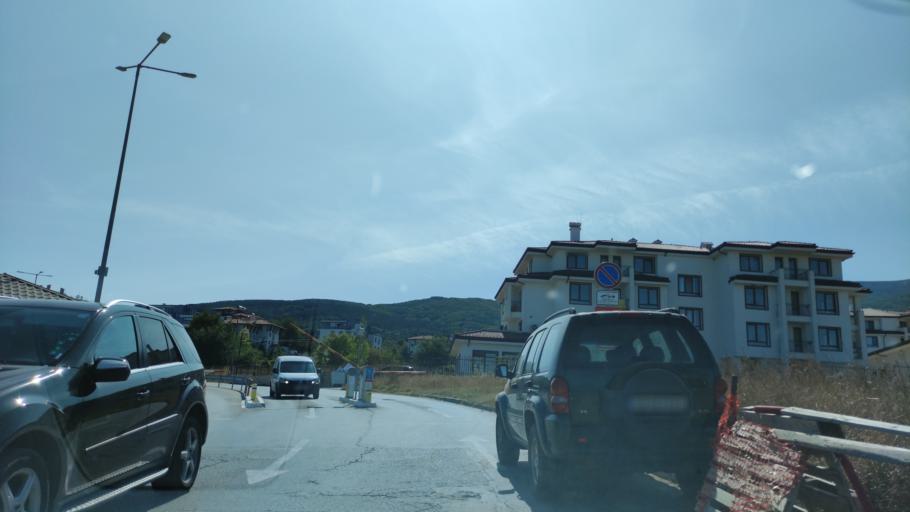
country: BG
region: Sofia-Capital
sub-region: Stolichna Obshtina
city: Sofia
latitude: 42.6181
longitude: 23.3485
